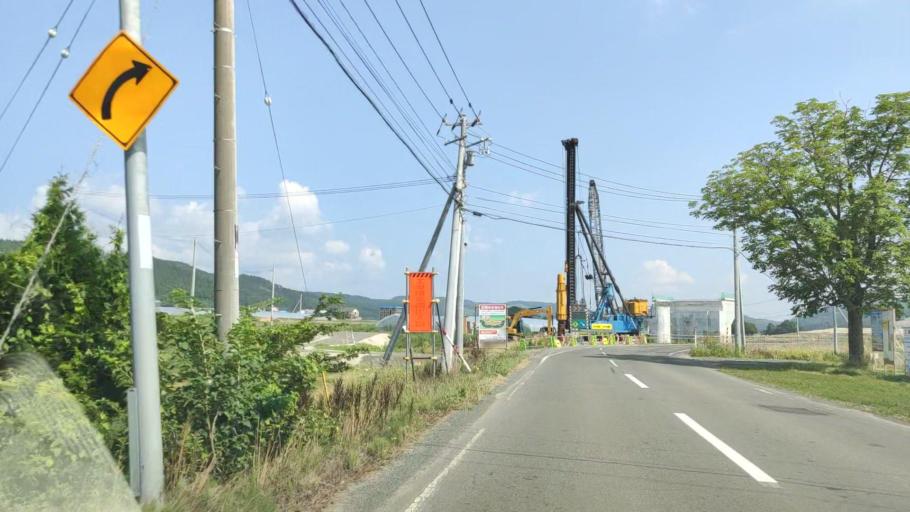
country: JP
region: Hokkaido
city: Shimo-furano
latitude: 43.3864
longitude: 142.3932
